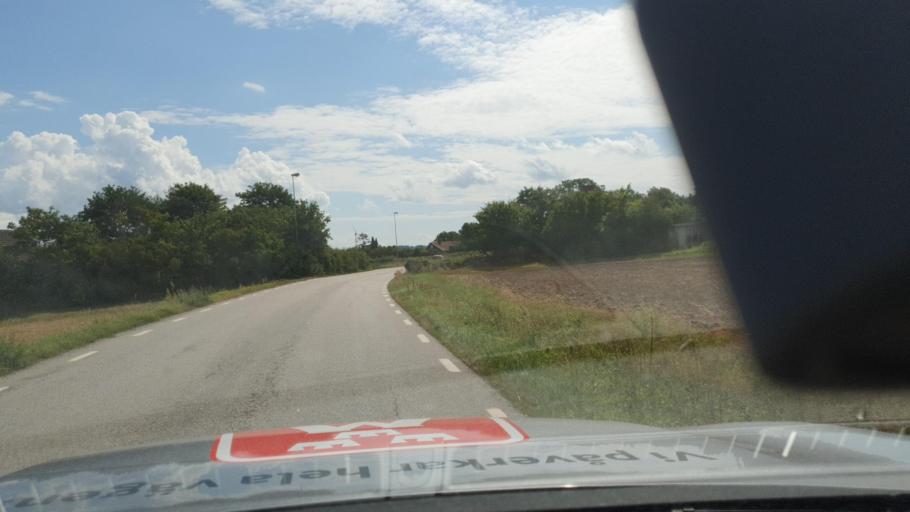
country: SE
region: Blekinge
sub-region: Solvesborgs Kommun
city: Soelvesborg
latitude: 56.0398
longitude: 14.6307
